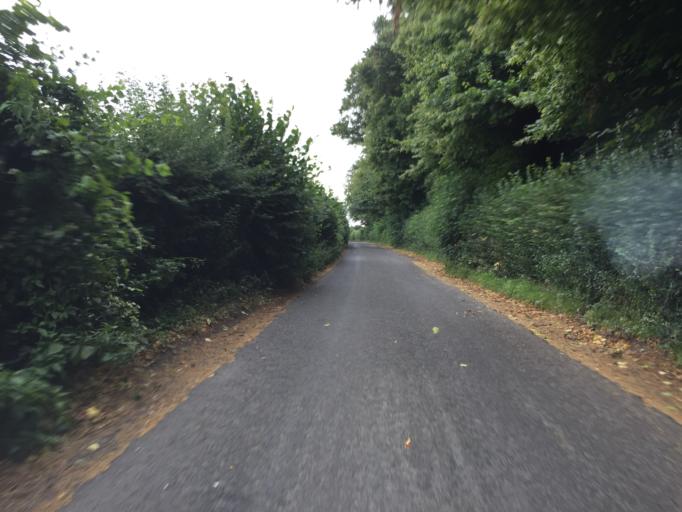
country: GB
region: England
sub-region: Kent
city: Maidstone
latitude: 51.2391
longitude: 0.5361
